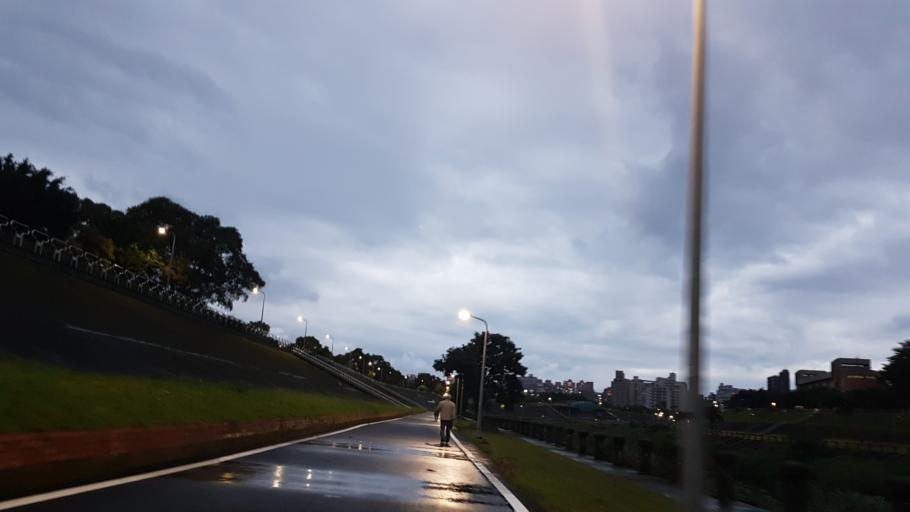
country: TW
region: Taipei
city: Taipei
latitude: 24.9803
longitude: 121.5641
